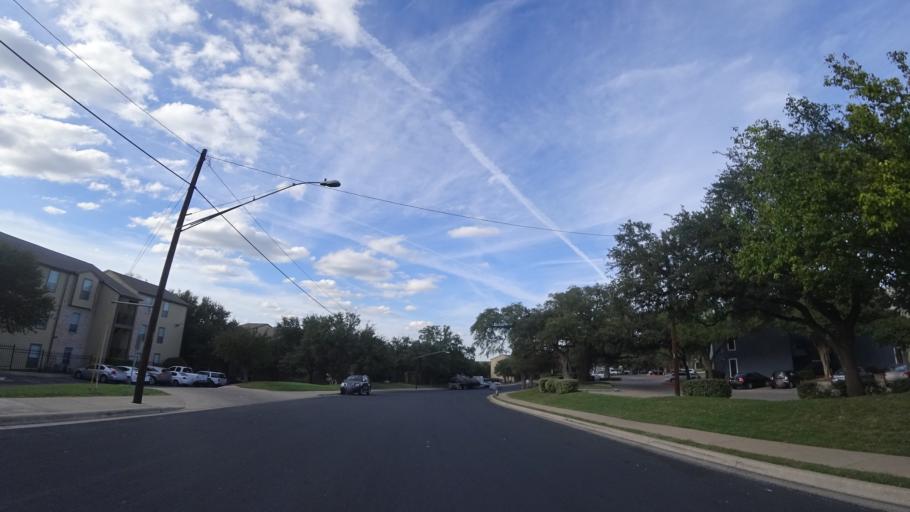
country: US
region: Texas
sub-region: Travis County
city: Onion Creek
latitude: 30.1930
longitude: -97.7643
